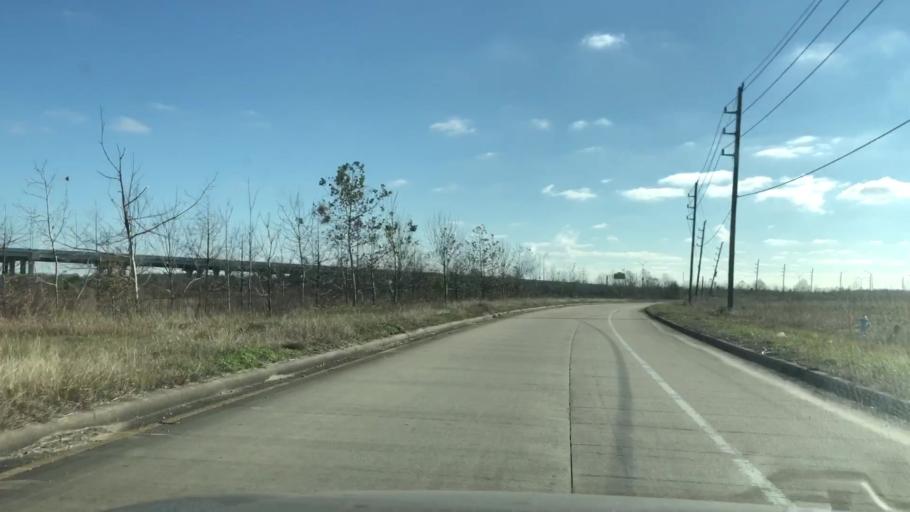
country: US
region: Texas
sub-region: Harris County
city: Cloverleaf
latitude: 29.8300
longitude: -95.1773
